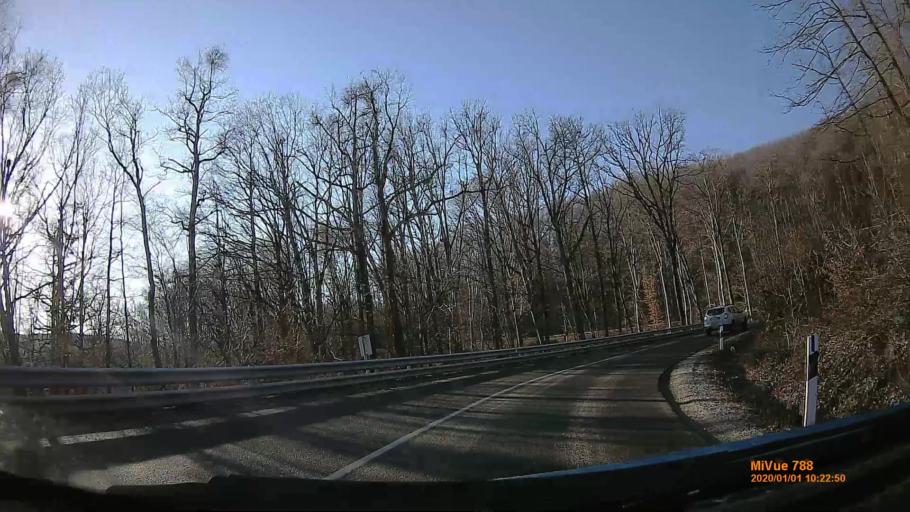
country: HU
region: Heves
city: Paradsasvar
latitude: 47.8945
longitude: 19.9786
